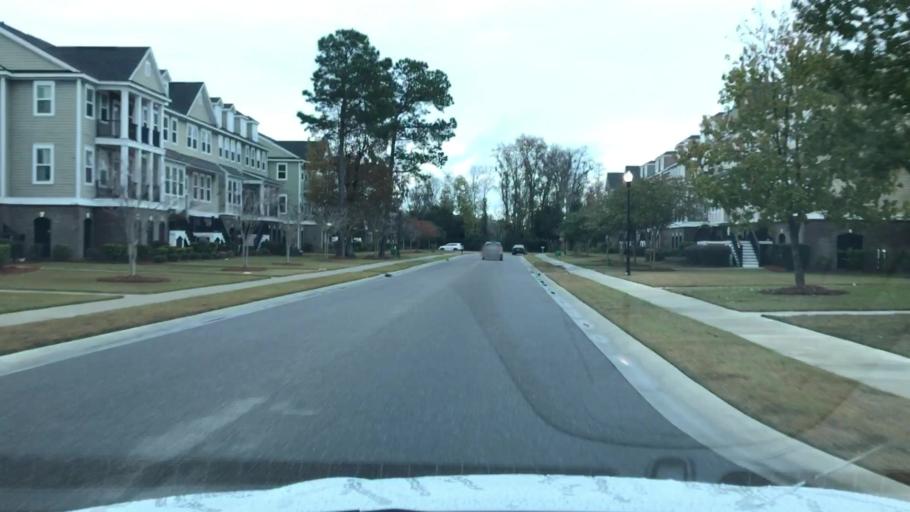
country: US
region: South Carolina
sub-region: Charleston County
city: Shell Point
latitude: 32.8083
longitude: -80.0532
